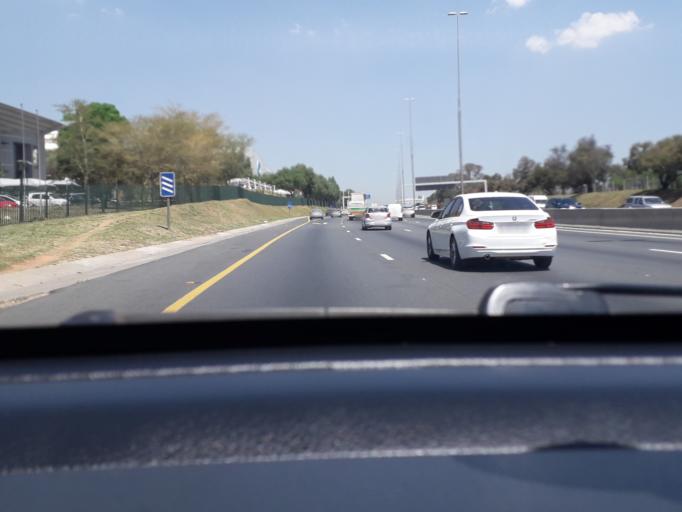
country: ZA
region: Gauteng
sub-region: City of Johannesburg Metropolitan Municipality
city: Modderfontein
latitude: -26.1108
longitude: 28.1304
